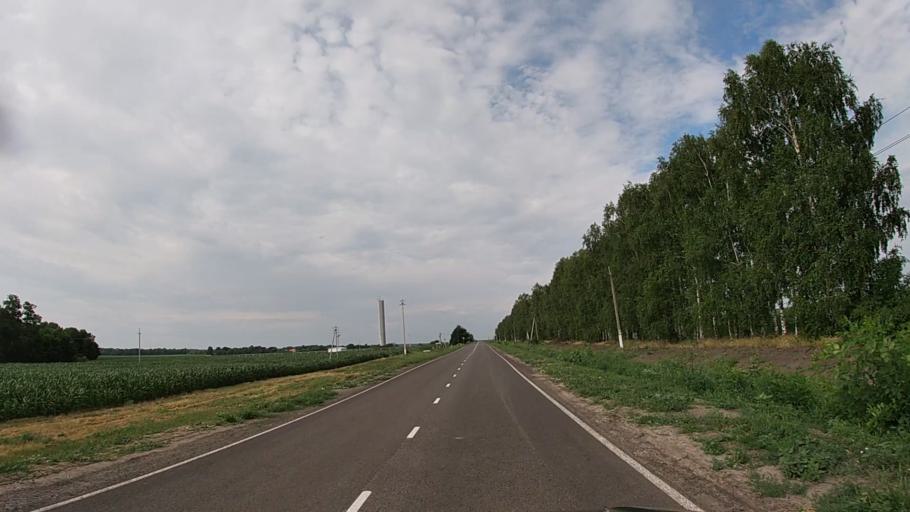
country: UA
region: Sumy
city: Krasnopillya
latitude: 50.8193
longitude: 35.4547
